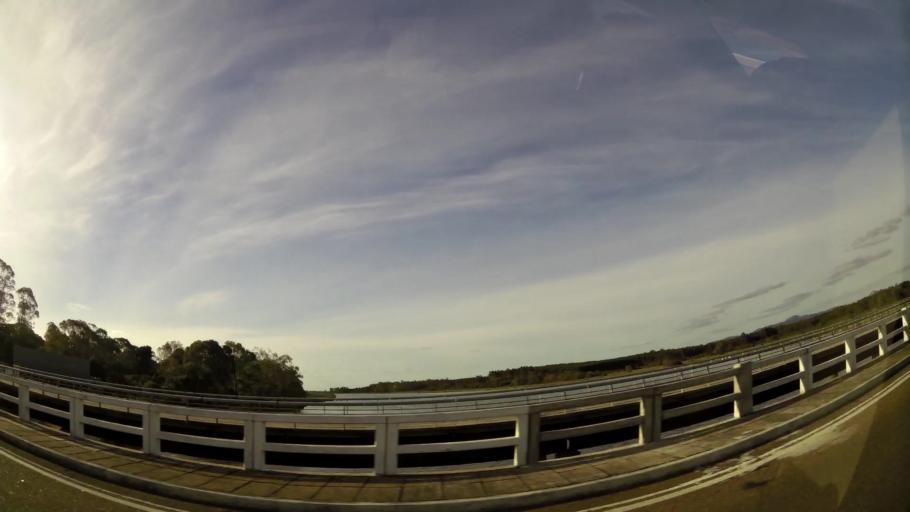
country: UY
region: Maldonado
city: Piriapolis
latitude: -34.7792
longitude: -55.3972
